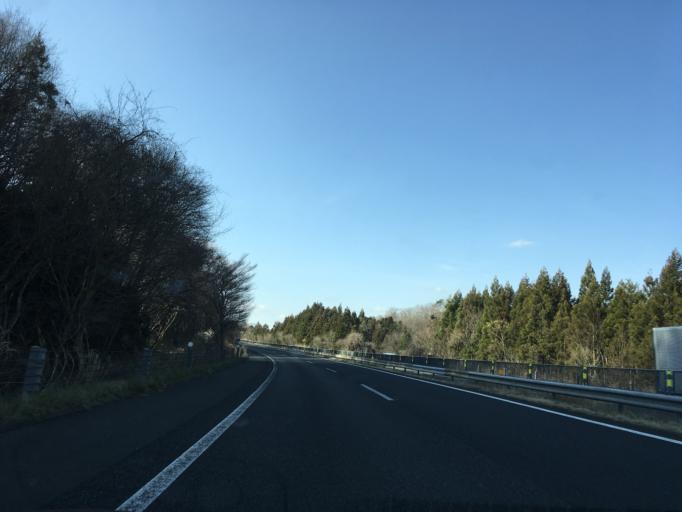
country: JP
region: Iwate
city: Ichinoseki
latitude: 38.8718
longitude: 141.0950
